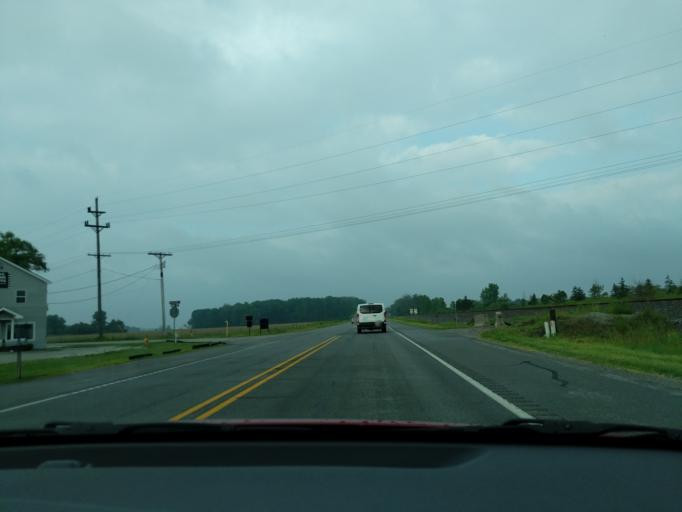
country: US
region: Indiana
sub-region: Hancock County
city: Fortville
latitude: 39.9265
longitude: -85.8620
